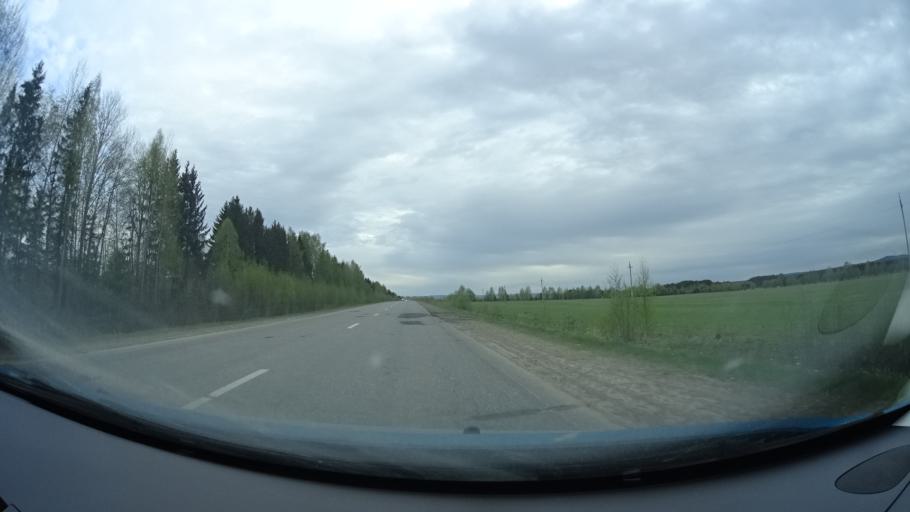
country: RU
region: Perm
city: Osa
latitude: 57.3454
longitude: 55.5916
